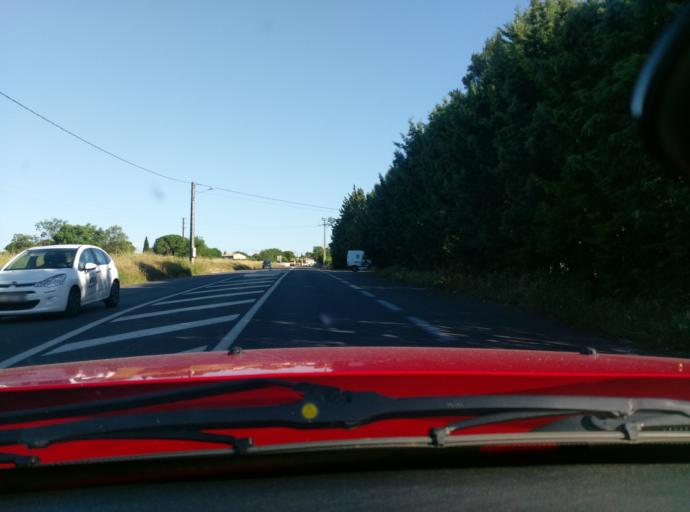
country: FR
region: Languedoc-Roussillon
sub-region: Departement du Gard
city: Uzes
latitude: 43.9961
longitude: 4.4173
